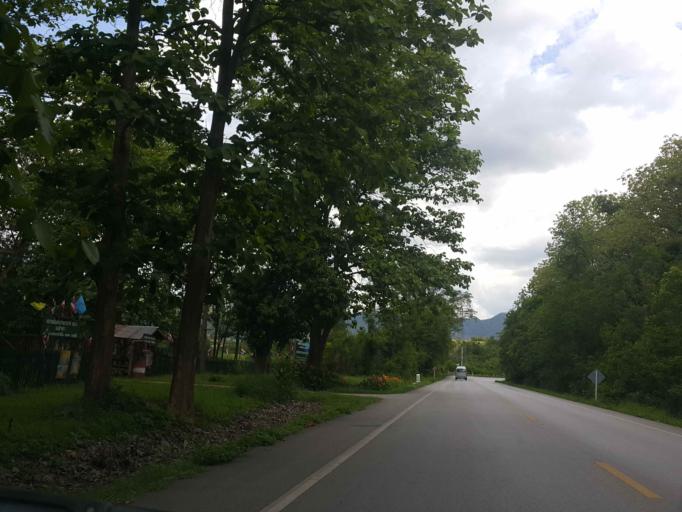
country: TH
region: Nan
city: Wiang Sa
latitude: 18.5220
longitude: 100.5788
